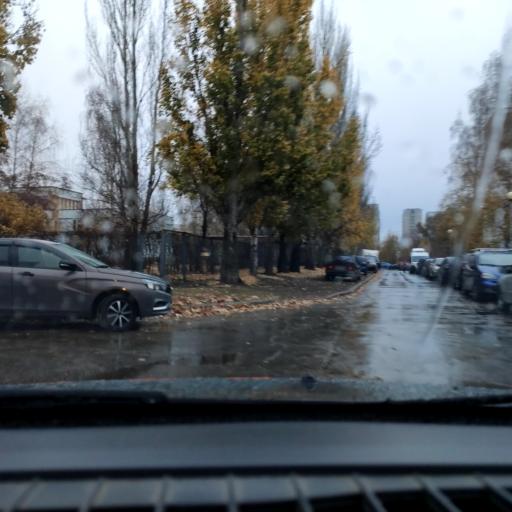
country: RU
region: Samara
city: Tol'yatti
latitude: 53.5305
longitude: 49.3297
